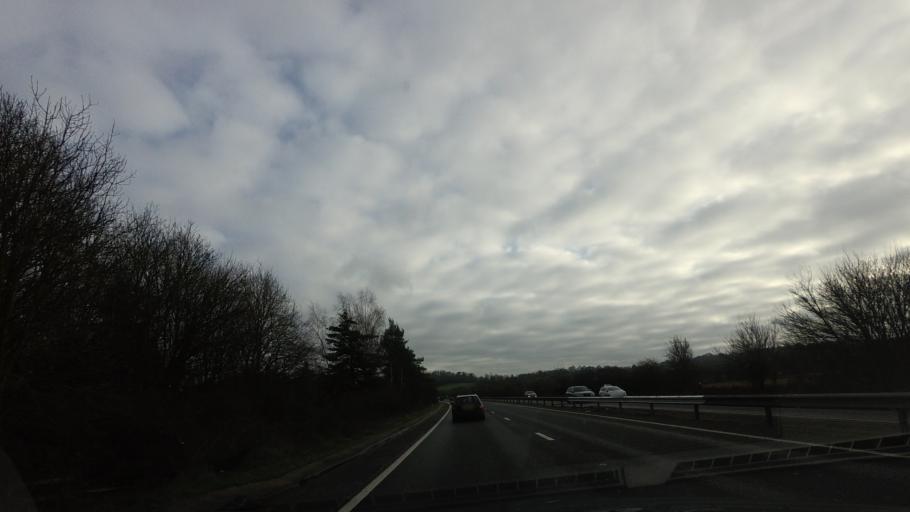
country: GB
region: England
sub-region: Kent
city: Tonbridge
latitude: 51.1851
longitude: 0.2427
